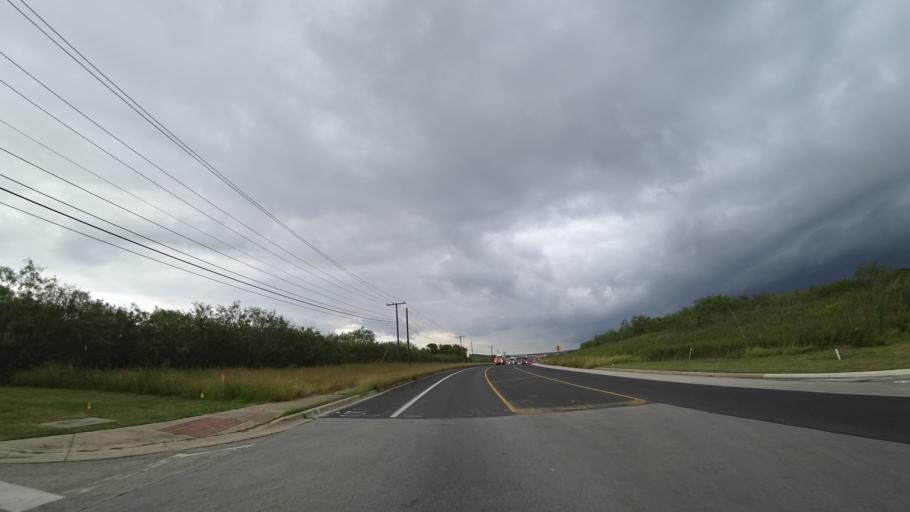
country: US
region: Texas
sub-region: Travis County
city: Onion Creek
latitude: 30.1643
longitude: -97.7282
